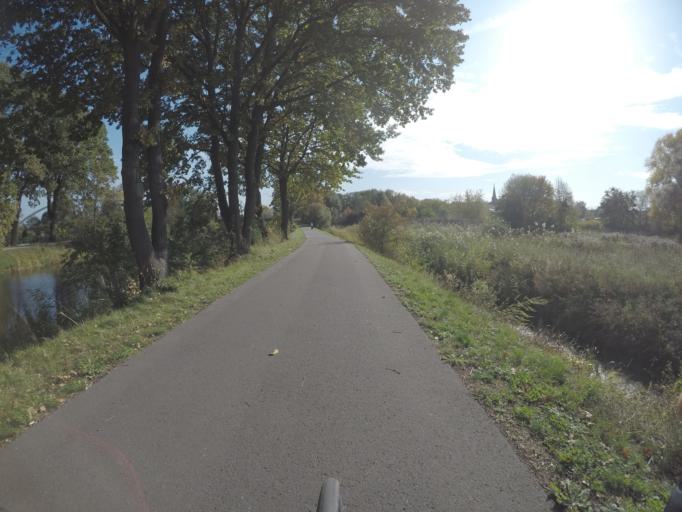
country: DE
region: Brandenburg
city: Hohen Neuendorf
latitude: 52.7061
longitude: 13.2470
